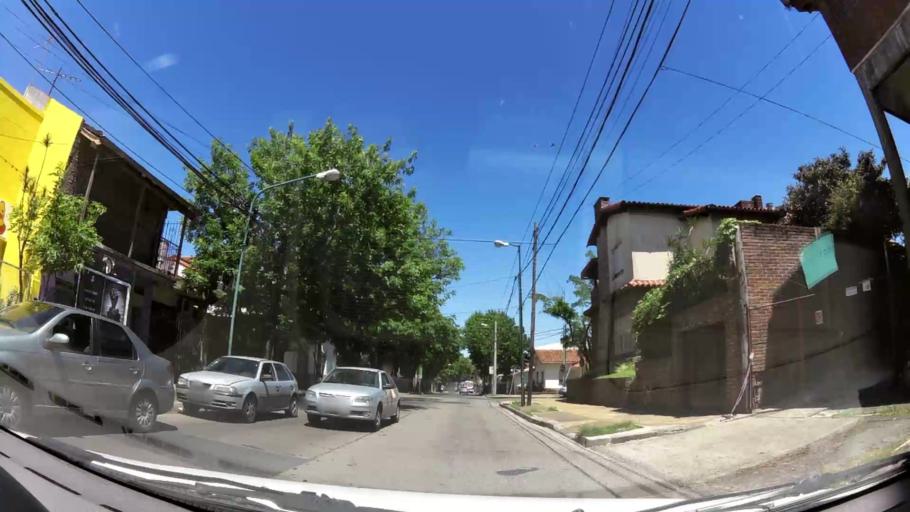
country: AR
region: Buenos Aires
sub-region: Partido de Vicente Lopez
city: Olivos
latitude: -34.4984
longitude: -58.4991
